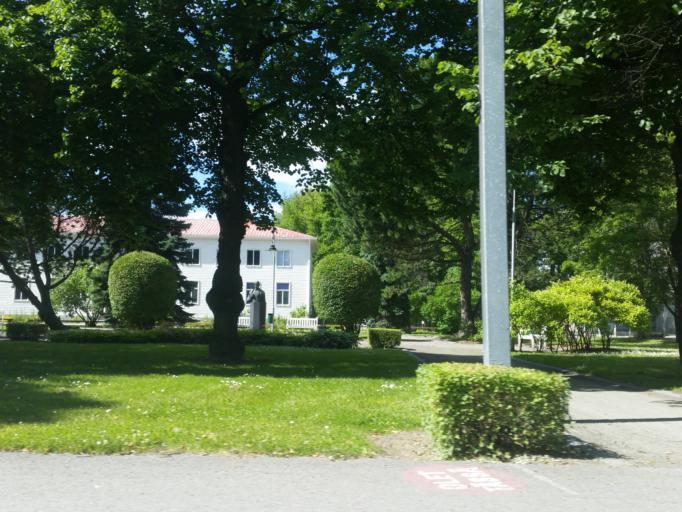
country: FI
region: Northern Savo
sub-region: Varkaus
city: Varkaus
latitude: 62.3175
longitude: 27.9001
